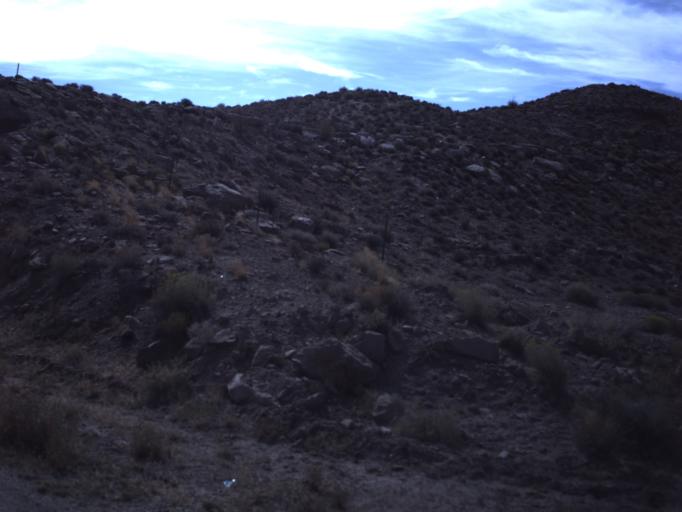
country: US
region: Utah
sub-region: San Juan County
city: Blanding
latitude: 37.3095
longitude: -109.3010
